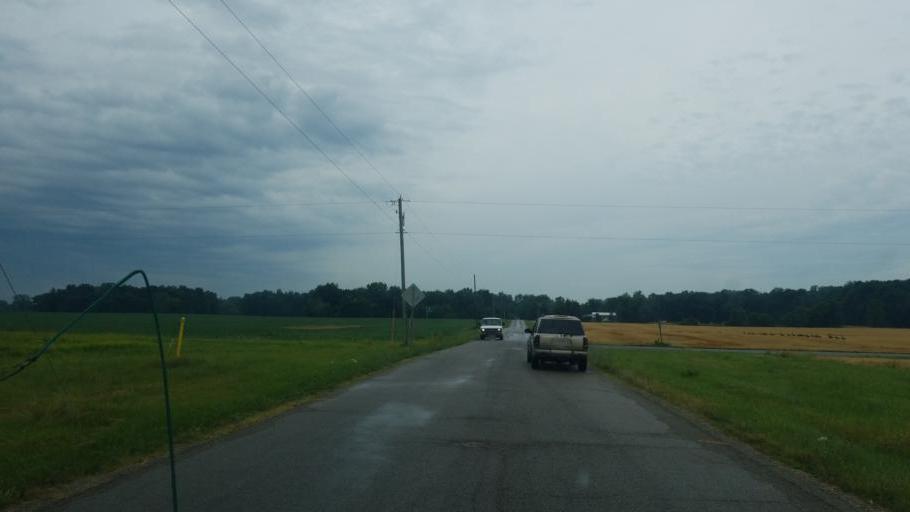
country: US
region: Ohio
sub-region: Williams County
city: Edgerton
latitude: 41.4427
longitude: -84.6706
